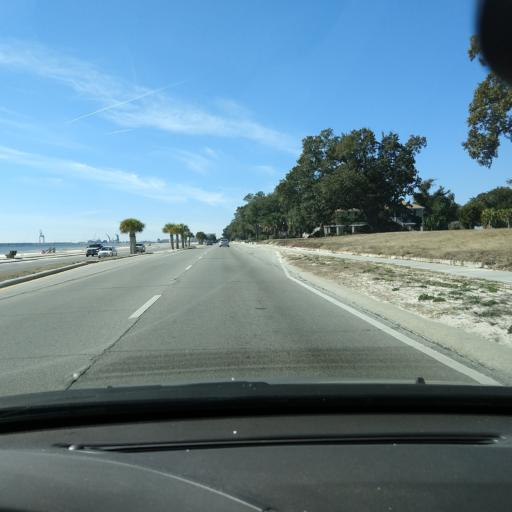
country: US
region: Mississippi
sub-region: Harrison County
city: Gulfport
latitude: 30.3735
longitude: -89.0673
